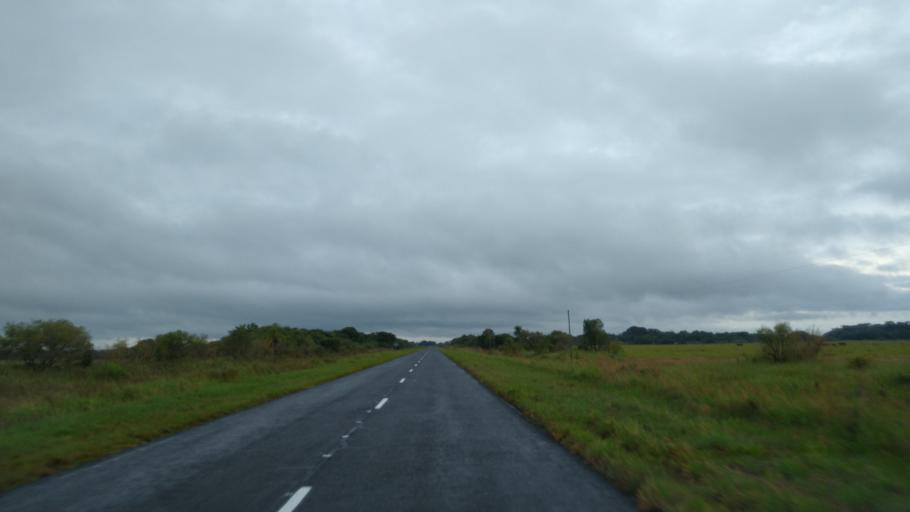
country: AR
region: Corrientes
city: Loreto
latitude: -27.6875
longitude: -57.2140
